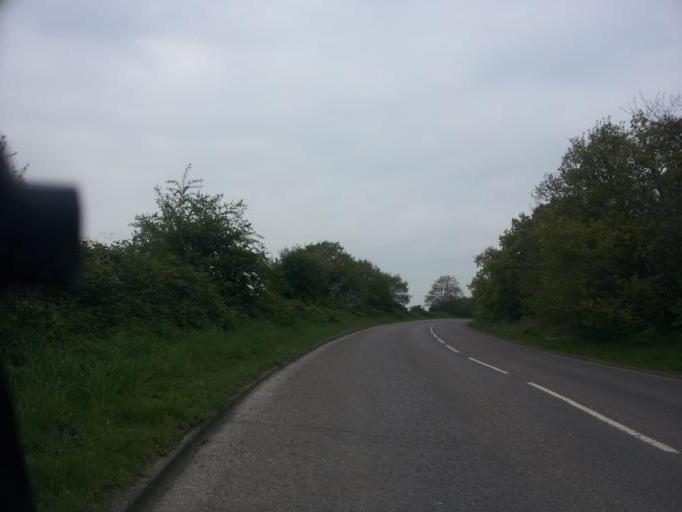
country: GB
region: England
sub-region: Medway
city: Rochester
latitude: 51.4119
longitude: 0.5240
